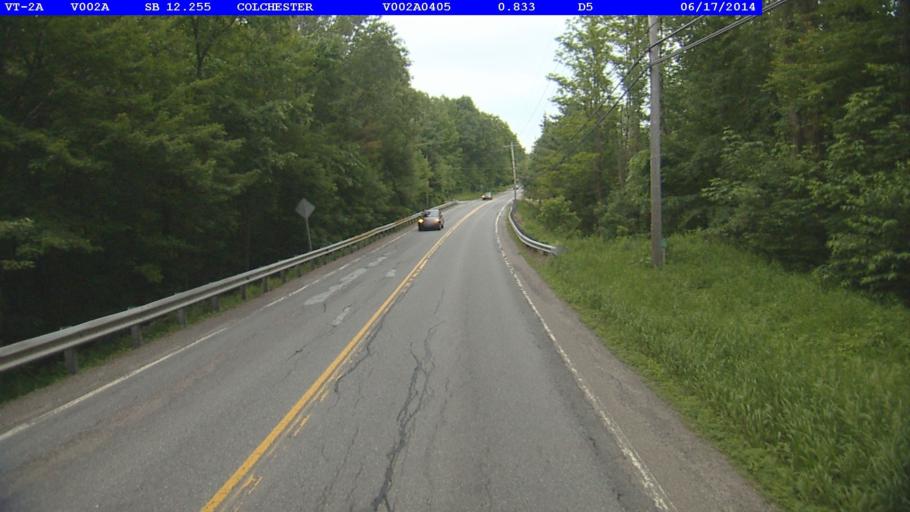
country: US
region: Vermont
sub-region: Chittenden County
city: Colchester
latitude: 44.5376
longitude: -73.1390
